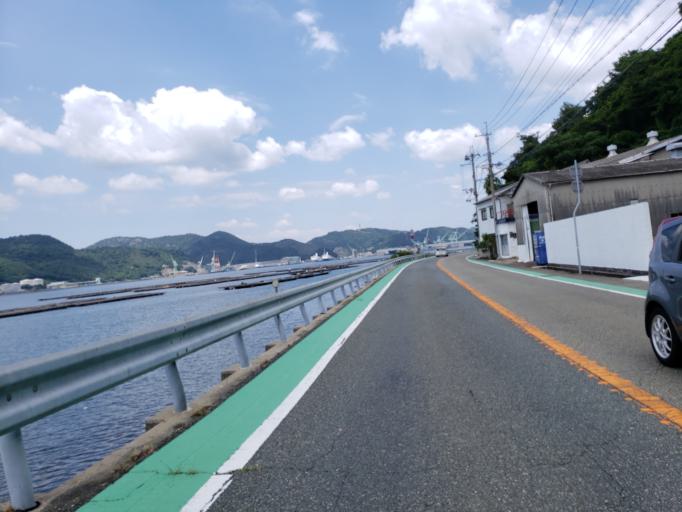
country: JP
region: Hyogo
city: Aioi
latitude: 34.7686
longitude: 134.4700
